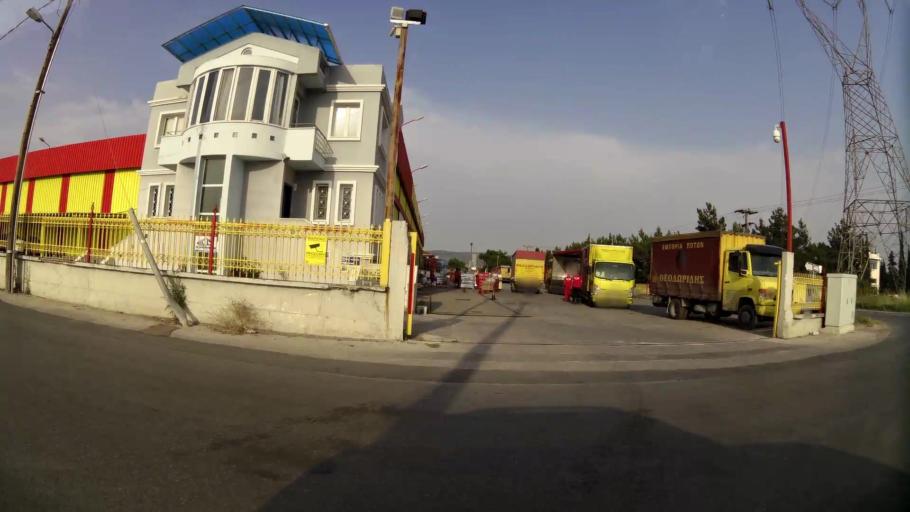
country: GR
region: Central Macedonia
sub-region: Nomos Thessalonikis
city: Oraiokastro
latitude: 40.7025
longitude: 22.9128
